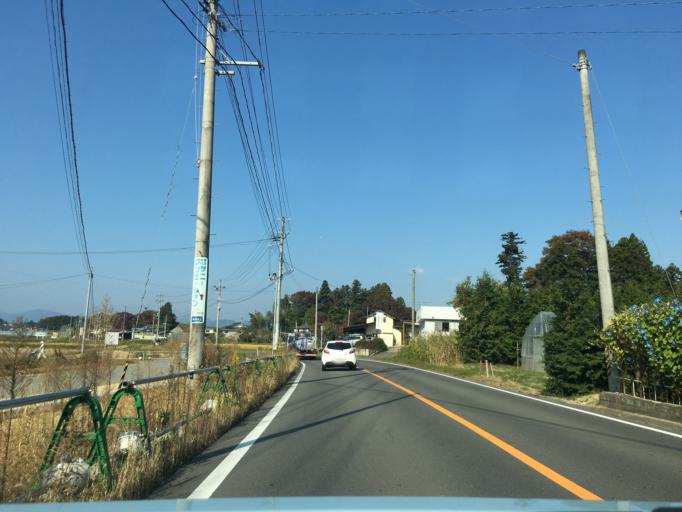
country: JP
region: Fukushima
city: Sukagawa
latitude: 37.2801
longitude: 140.3153
